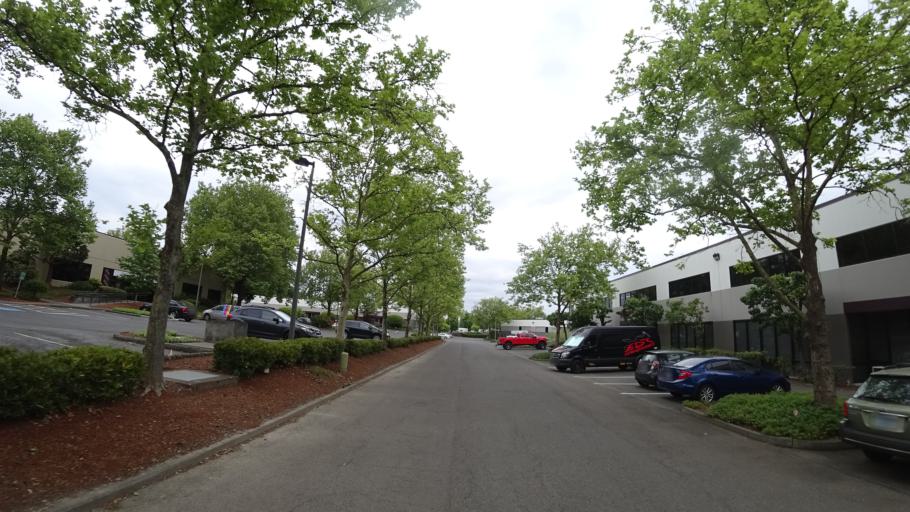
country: US
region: Oregon
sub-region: Washington County
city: Raleigh Hills
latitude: 45.4754
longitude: -122.7770
